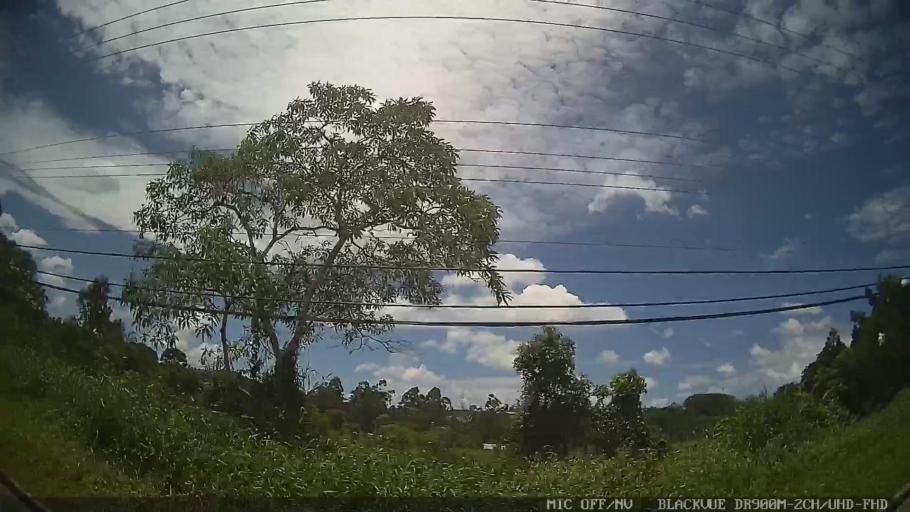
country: BR
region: Sao Paulo
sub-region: Biritiba-Mirim
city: Biritiba Mirim
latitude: -23.5503
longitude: -45.9686
